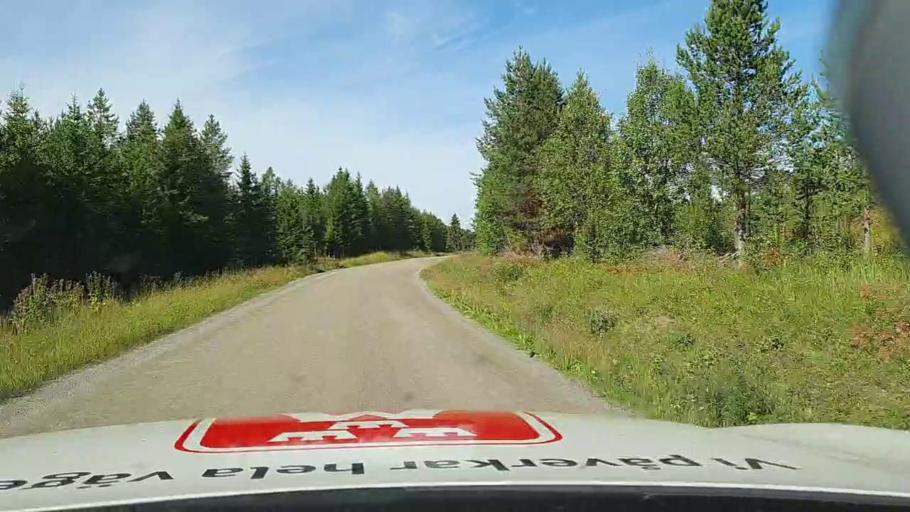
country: SE
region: Jaemtland
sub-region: Stroemsunds Kommun
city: Stroemsund
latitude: 63.6882
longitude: 15.3871
